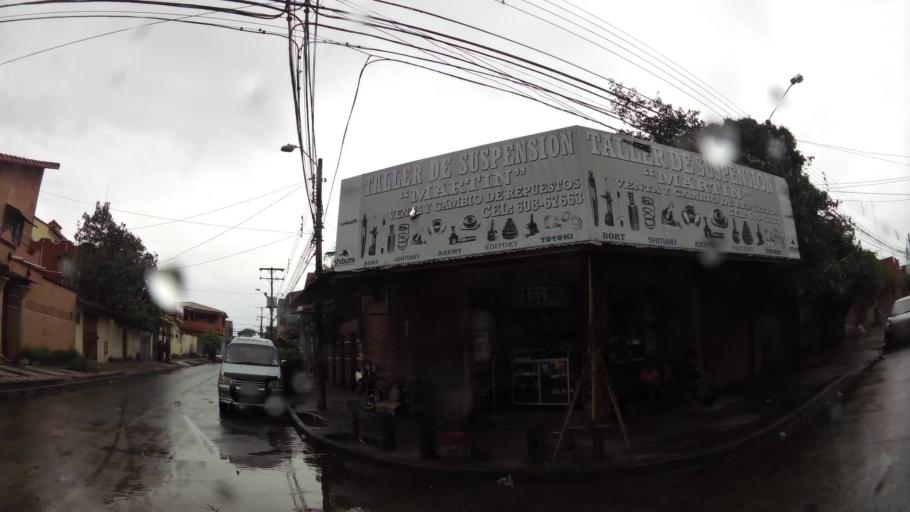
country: BO
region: Santa Cruz
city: Santa Cruz de la Sierra
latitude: -17.8145
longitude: -63.1889
